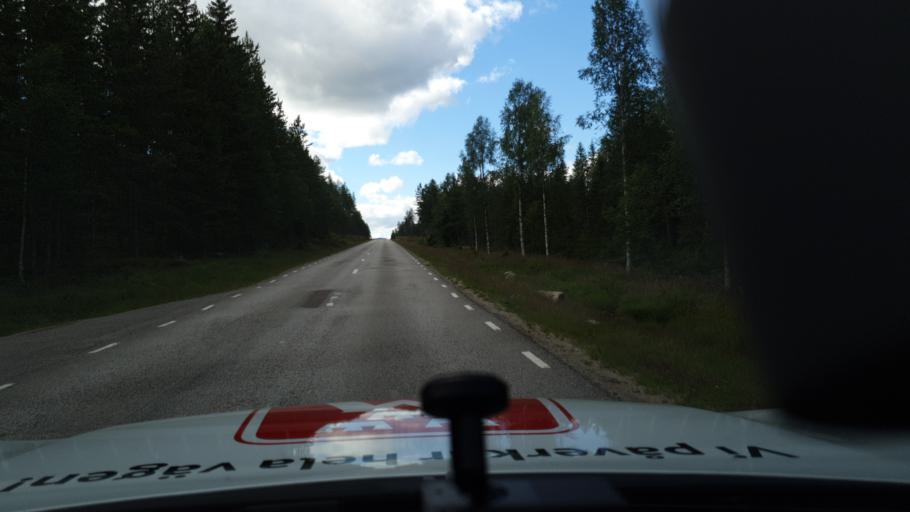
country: NO
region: Hedmark
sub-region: Trysil
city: Innbygda
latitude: 61.0196
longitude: 12.5172
